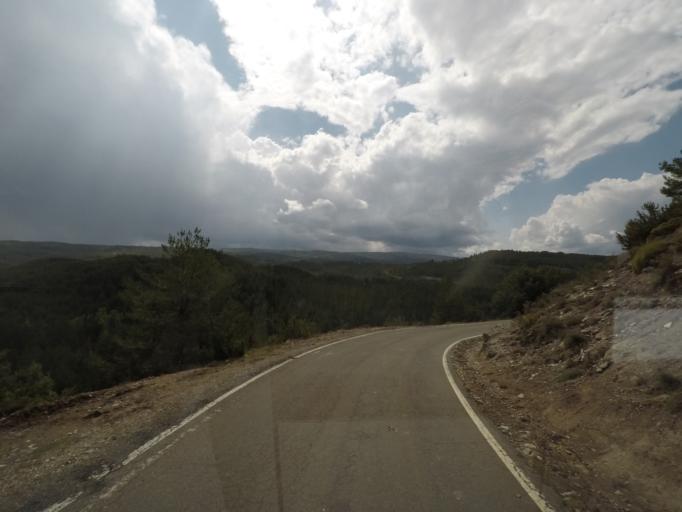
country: ES
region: Aragon
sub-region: Provincia de Huesca
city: Fiscal
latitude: 42.4075
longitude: -0.1378
